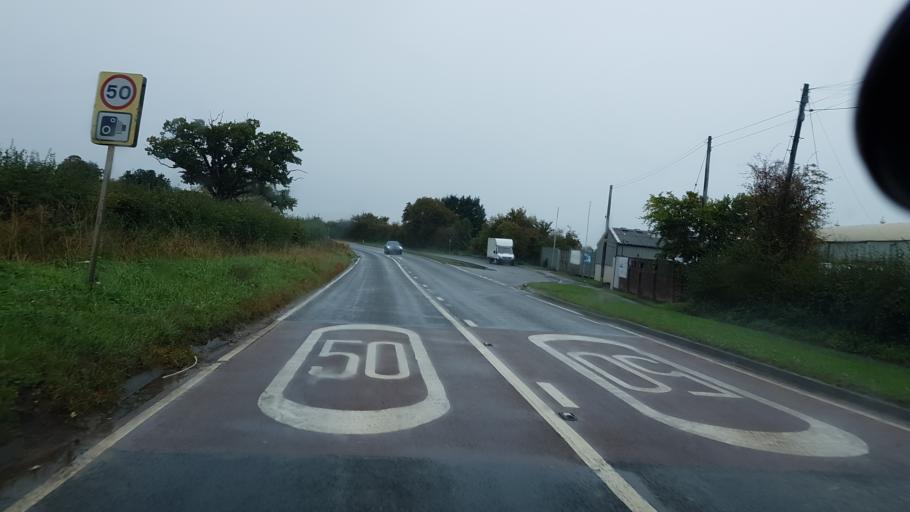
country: GB
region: England
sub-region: Worcestershire
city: Upton upon Severn
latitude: 52.0604
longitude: -2.1932
